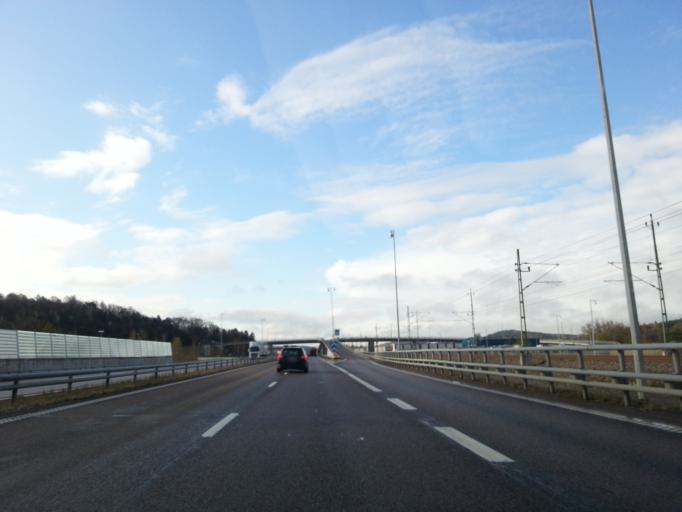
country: SE
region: Vaestra Goetaland
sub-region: Ale Kommun
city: Surte
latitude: 57.8379
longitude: 12.0130
